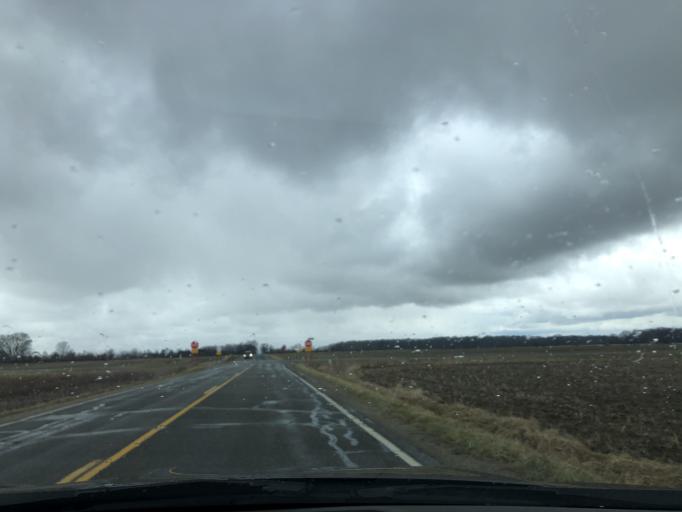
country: US
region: Michigan
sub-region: Clinton County
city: Fowler
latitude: 42.9295
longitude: -84.6599
